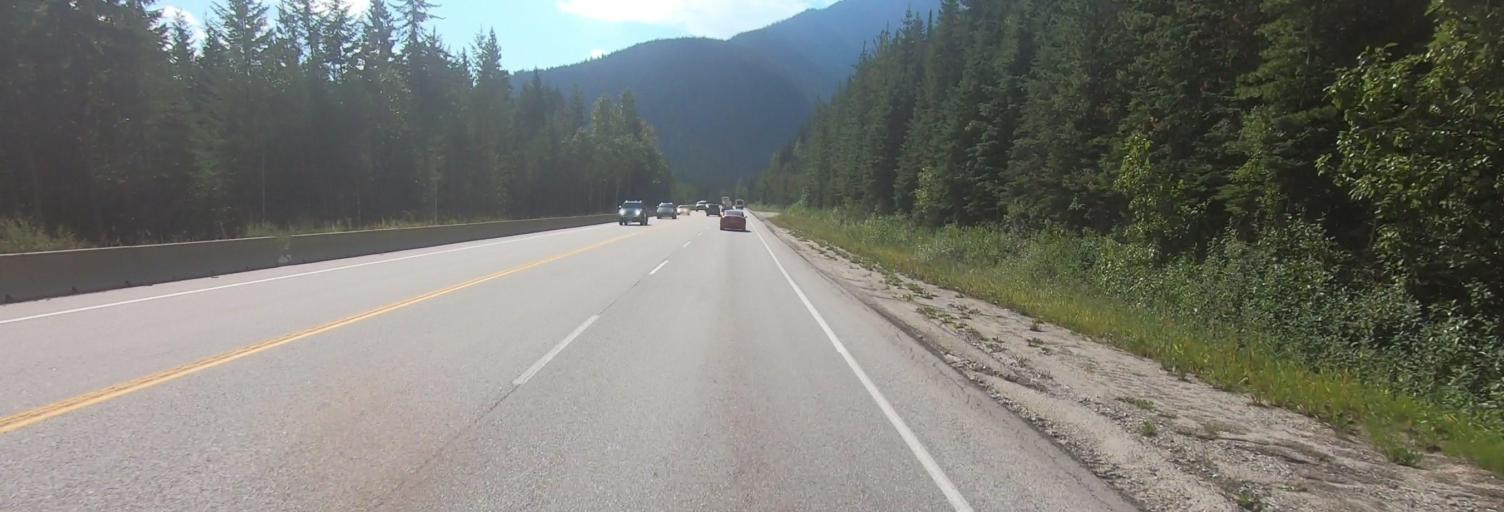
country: CA
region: British Columbia
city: Golden
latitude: 51.3517
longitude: -117.4363
